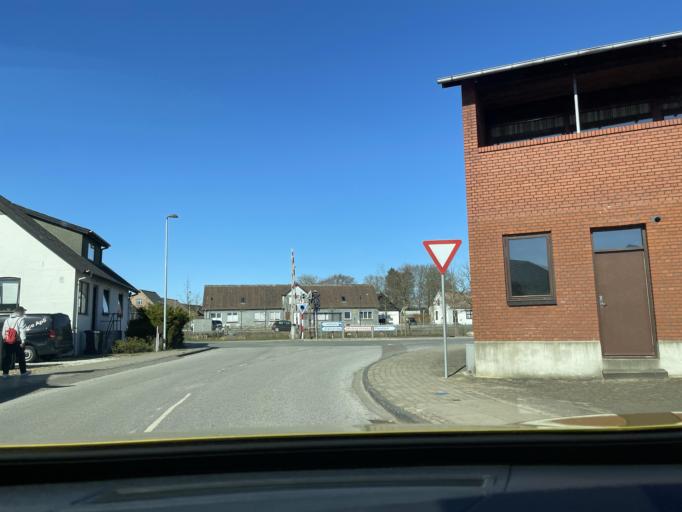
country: DK
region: Central Jutland
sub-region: Ikast-Brande Kommune
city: Bording Kirkeby
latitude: 56.1465
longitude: 9.2764
